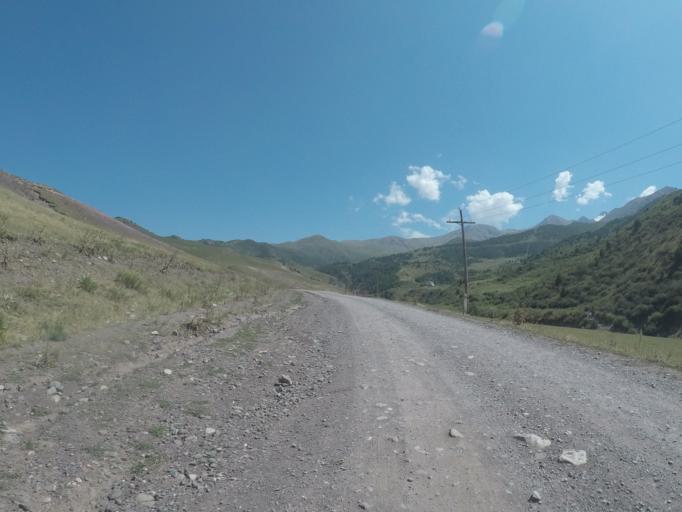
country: KG
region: Chuy
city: Bishkek
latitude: 42.6499
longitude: 74.5090
